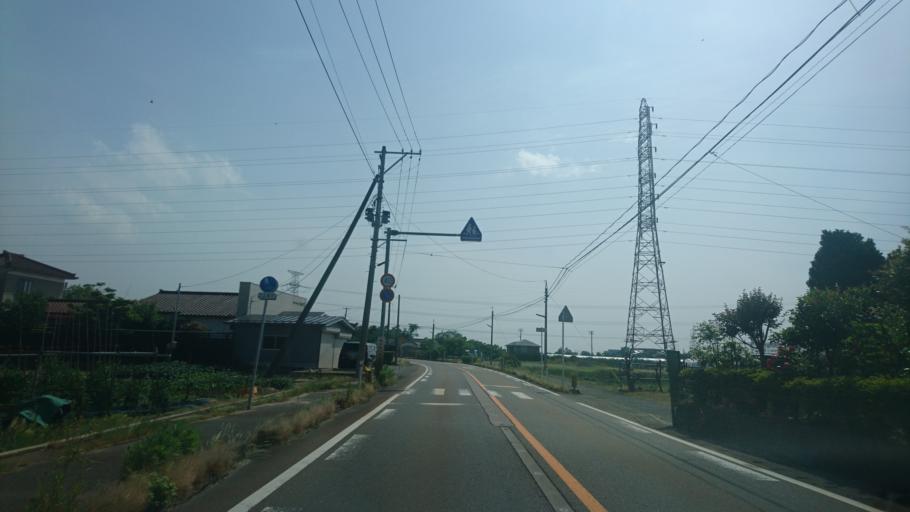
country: JP
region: Niigata
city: Shibata
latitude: 37.9819
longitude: 139.2911
